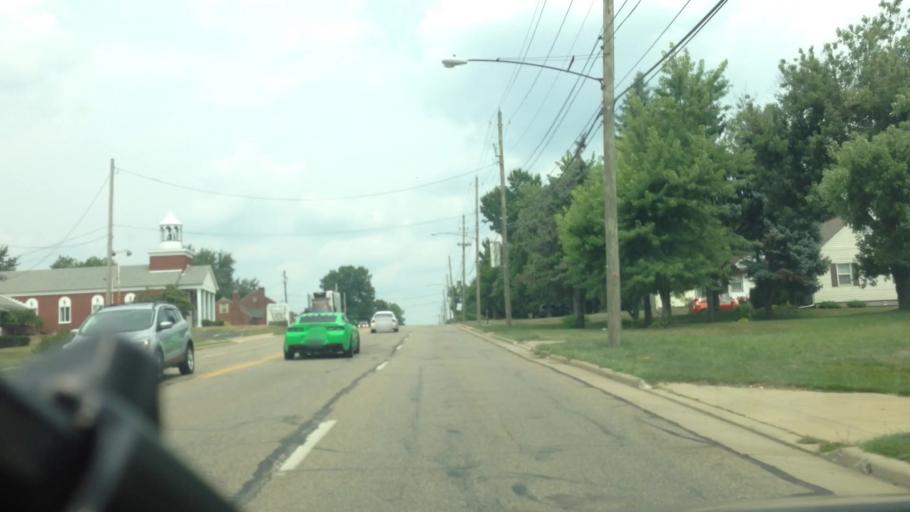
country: US
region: Ohio
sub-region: Stark County
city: Genoa
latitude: 40.7986
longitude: -81.4262
